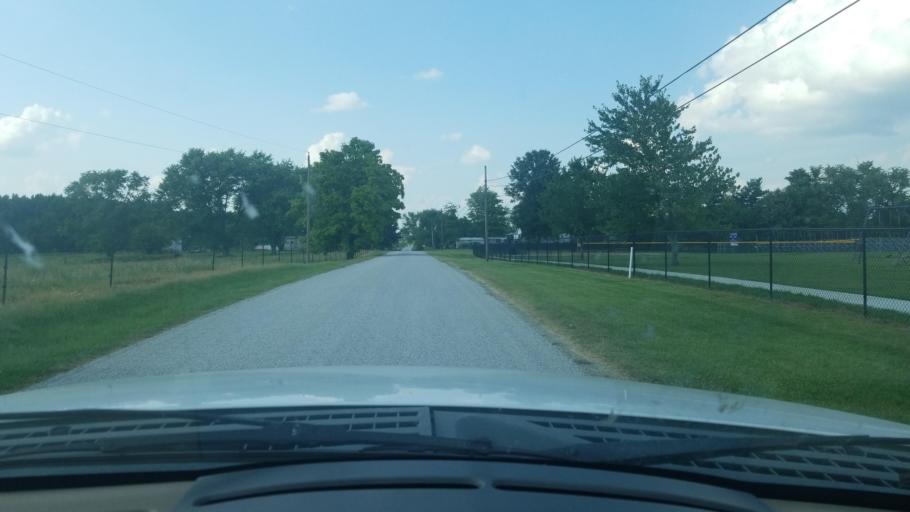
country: US
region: Illinois
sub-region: Saline County
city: Eldorado
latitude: 37.8275
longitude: -88.4385
